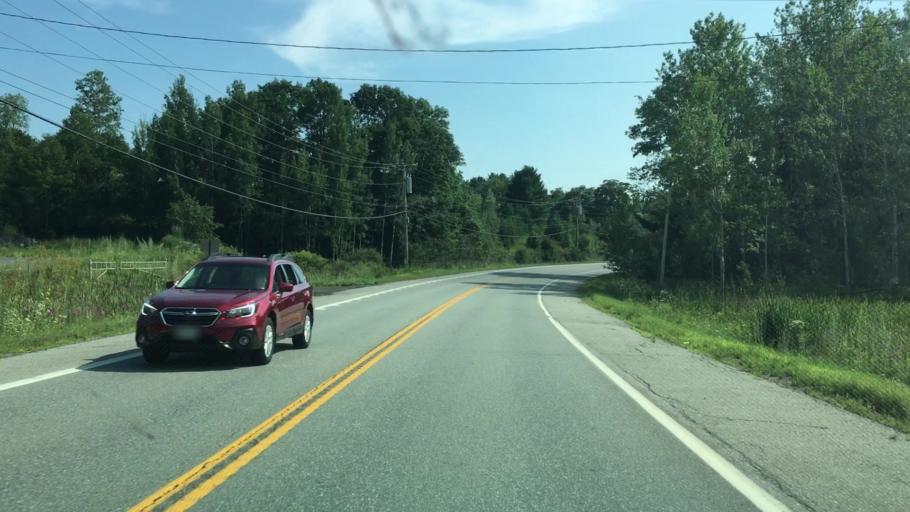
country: US
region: Maine
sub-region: Waldo County
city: Frankfort
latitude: 44.6252
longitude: -68.8689
